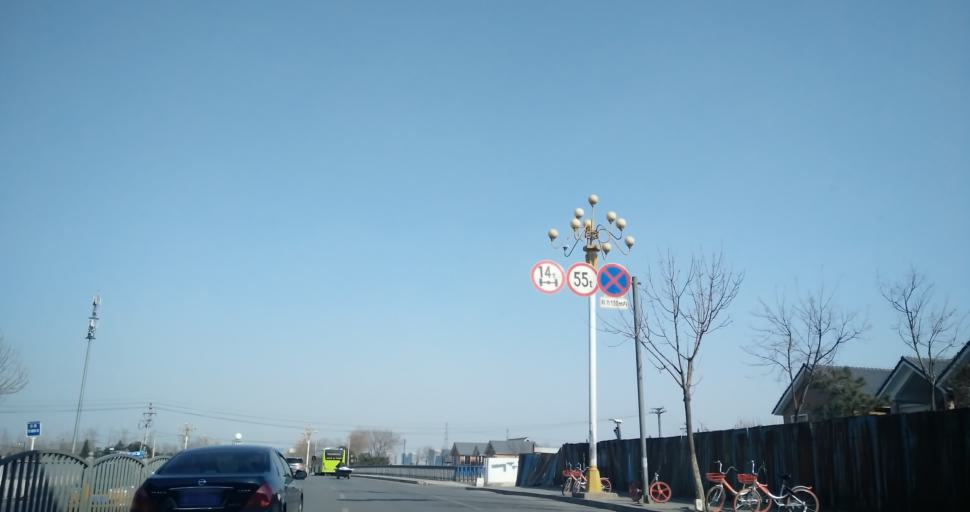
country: CN
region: Beijing
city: Jiugong
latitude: 39.8047
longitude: 116.4551
